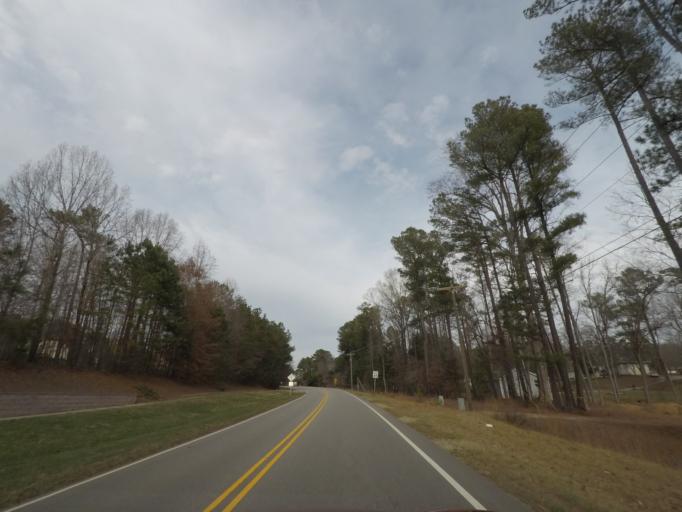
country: US
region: North Carolina
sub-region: Durham County
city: Durham
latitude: 36.0702
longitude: -78.9740
